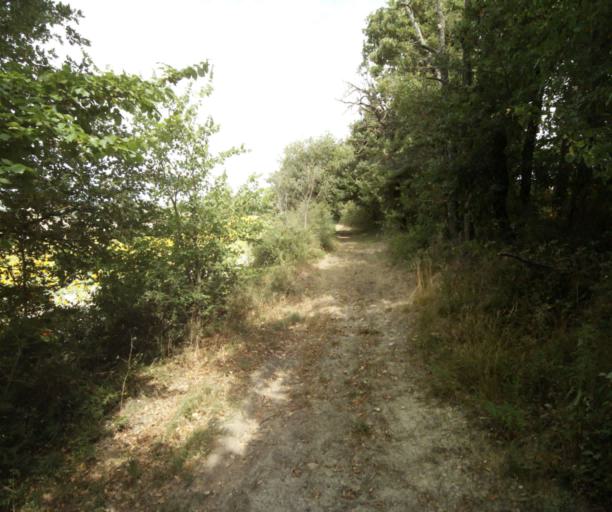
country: FR
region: Midi-Pyrenees
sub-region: Departement de la Haute-Garonne
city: Saint-Felix-Lauragais
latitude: 43.4249
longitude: 1.9286
